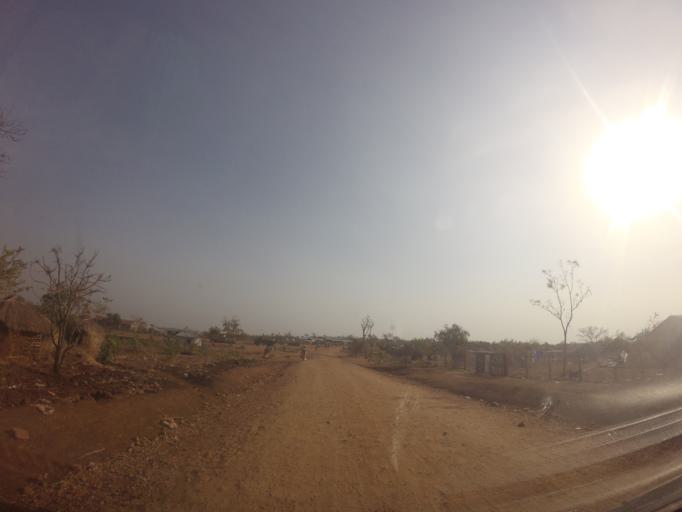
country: UG
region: Northern Region
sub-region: Maracha District
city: Maracha
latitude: 3.1239
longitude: 31.1601
